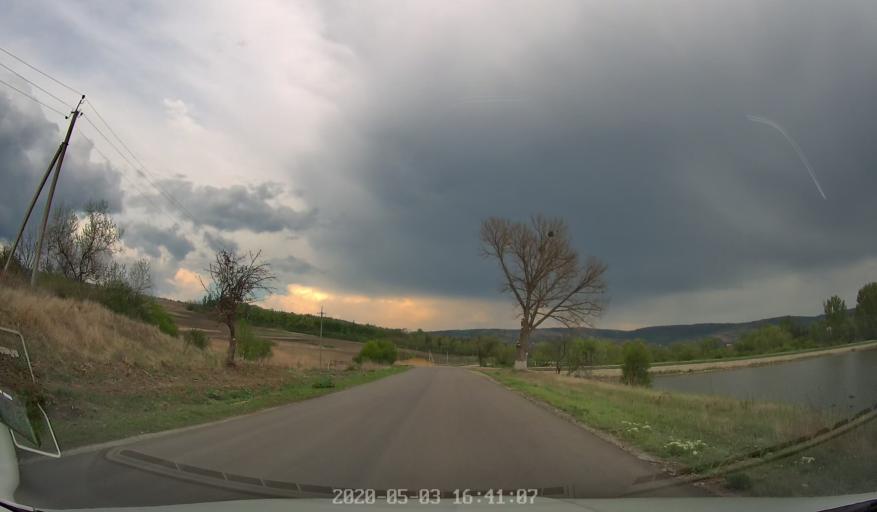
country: MD
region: Stinga Nistrului
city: Bucovat
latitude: 47.1695
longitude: 28.4033
